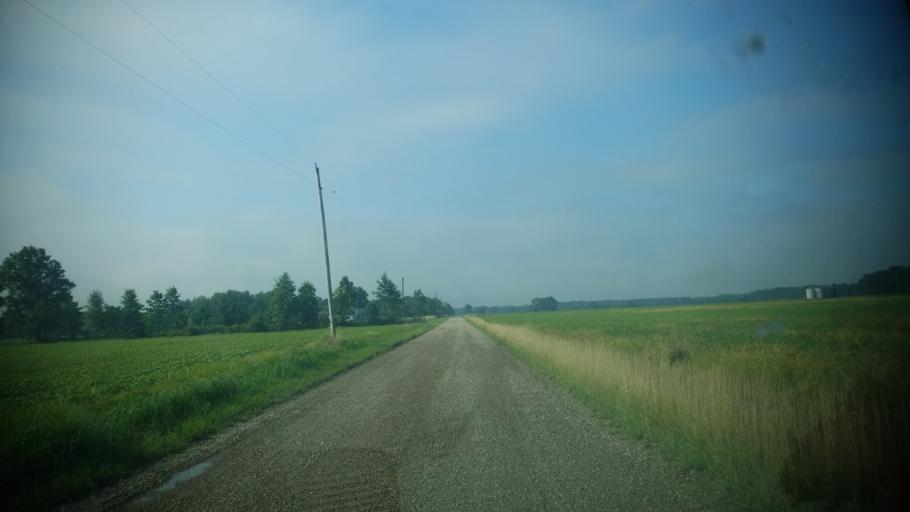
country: US
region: Illinois
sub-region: Clay County
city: Flora
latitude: 38.5983
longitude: -88.3643
